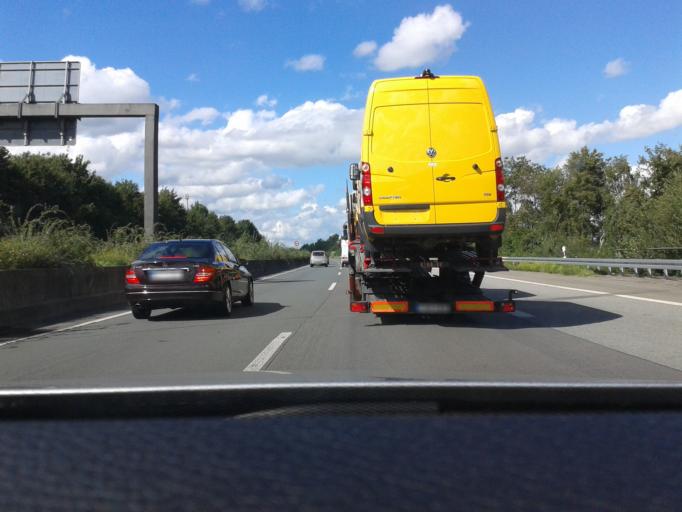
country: DE
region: North Rhine-Westphalia
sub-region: Regierungsbezirk Dusseldorf
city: Moers
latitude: 51.4417
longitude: 6.6021
